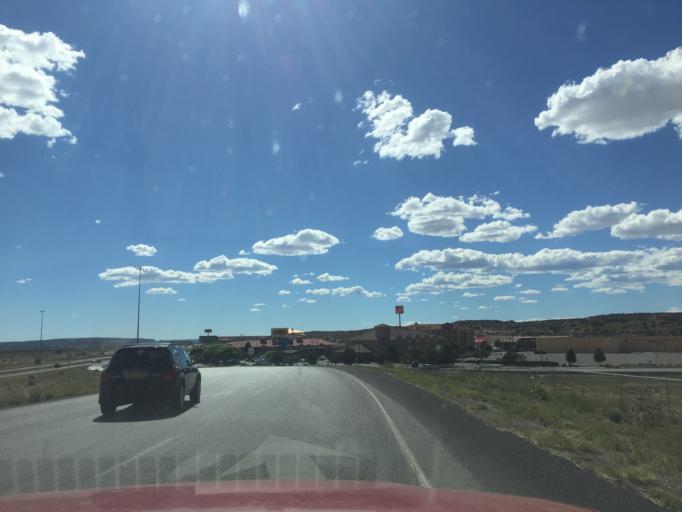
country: US
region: New Mexico
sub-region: McKinley County
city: Gallup
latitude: 35.5292
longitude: -108.7604
